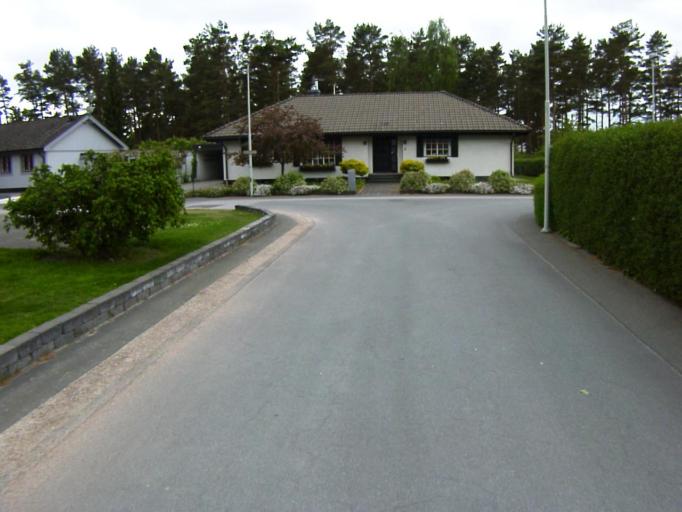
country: SE
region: Skane
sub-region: Kristianstads Kommun
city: Ahus
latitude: 55.9409
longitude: 14.2744
